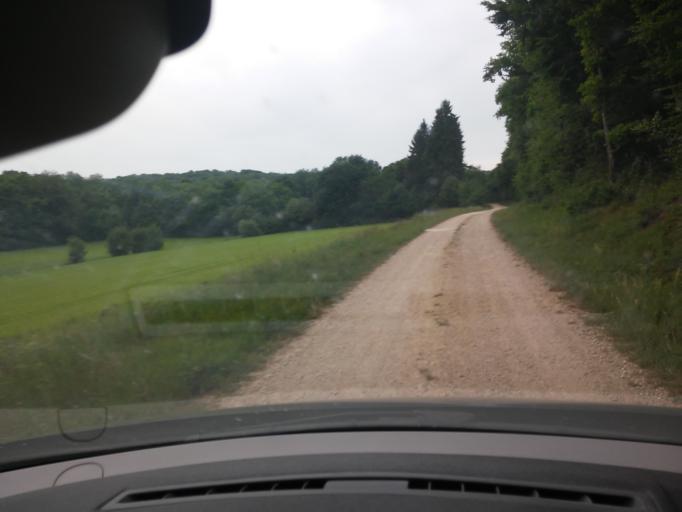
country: FR
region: Lorraine
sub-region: Departement de la Meuse
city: Saint-Mihiel
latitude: 48.9090
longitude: 5.4506
